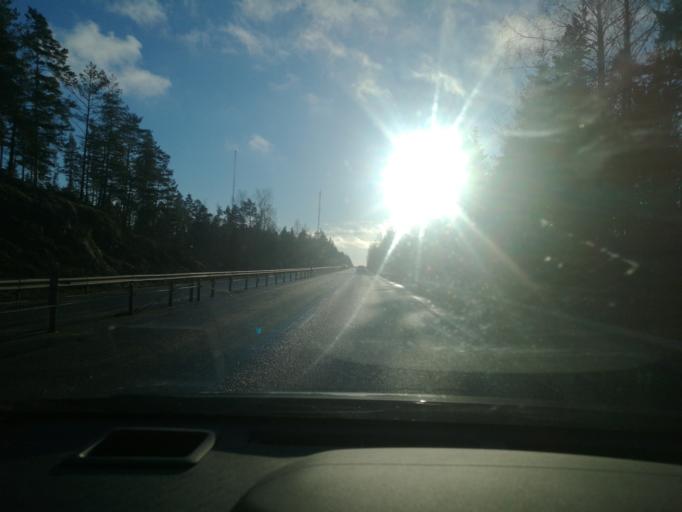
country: SE
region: OEstergoetland
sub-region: Norrkopings Kommun
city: Jursla
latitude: 58.7146
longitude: 16.1634
